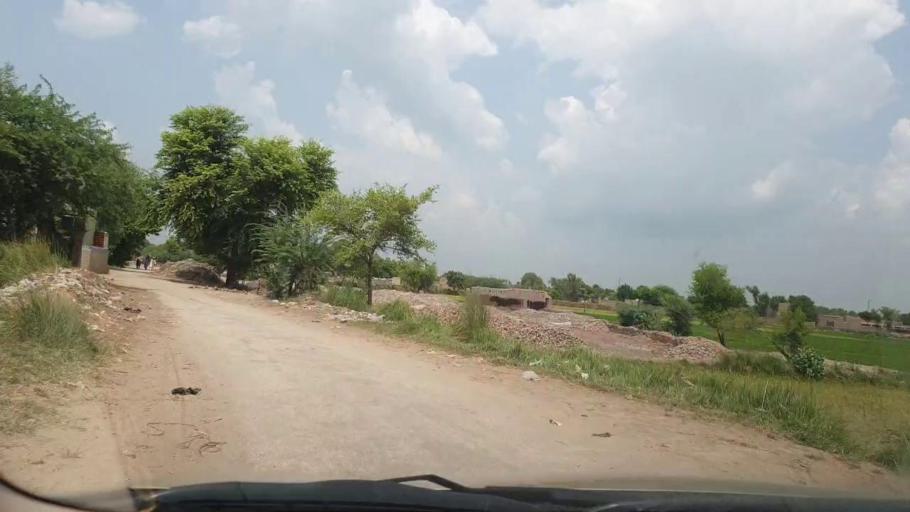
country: PK
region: Sindh
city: Larkana
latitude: 27.5746
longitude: 68.1225
